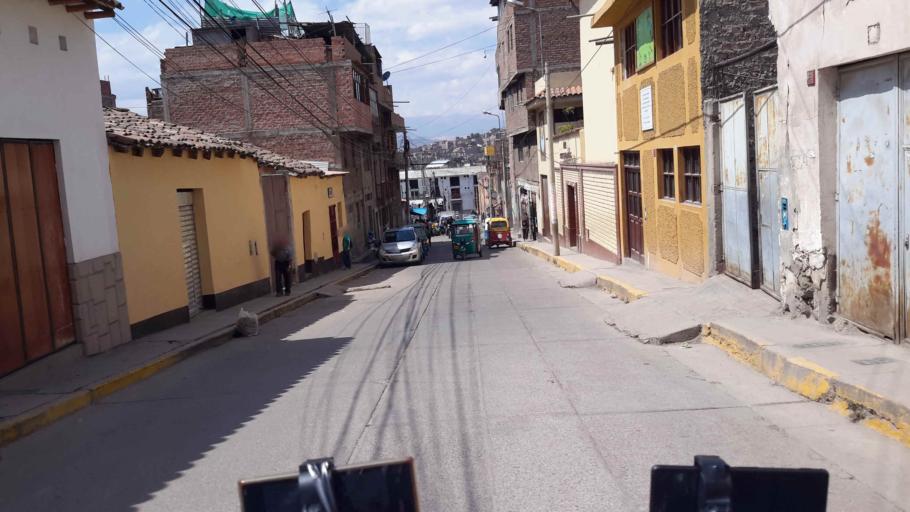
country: PE
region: Ayacucho
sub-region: Provincia de Huamanga
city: Ayacucho
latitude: -13.1652
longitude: -74.2294
